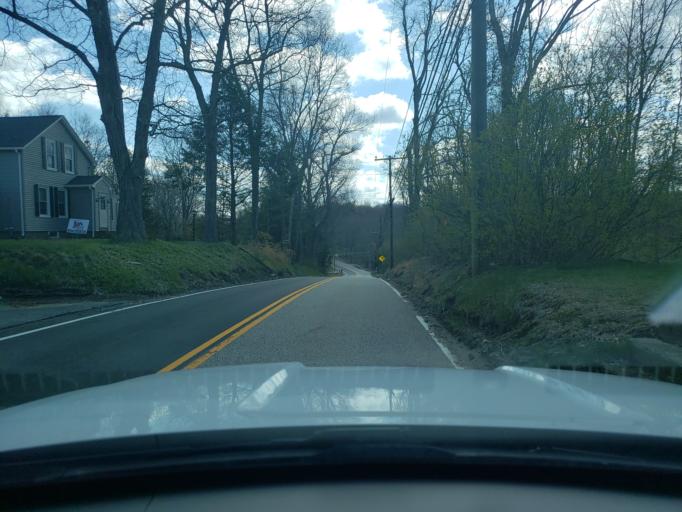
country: US
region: Connecticut
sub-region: New London County
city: Lisbon
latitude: 41.6052
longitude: -72.0019
